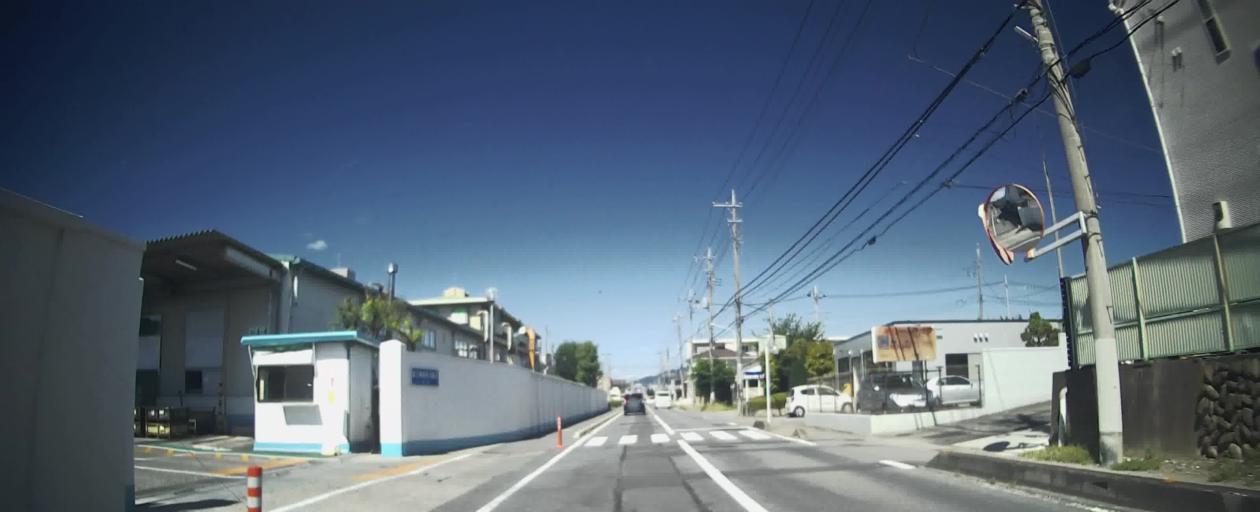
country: JP
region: Gunma
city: Maebashi-shi
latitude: 36.4025
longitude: 139.0551
